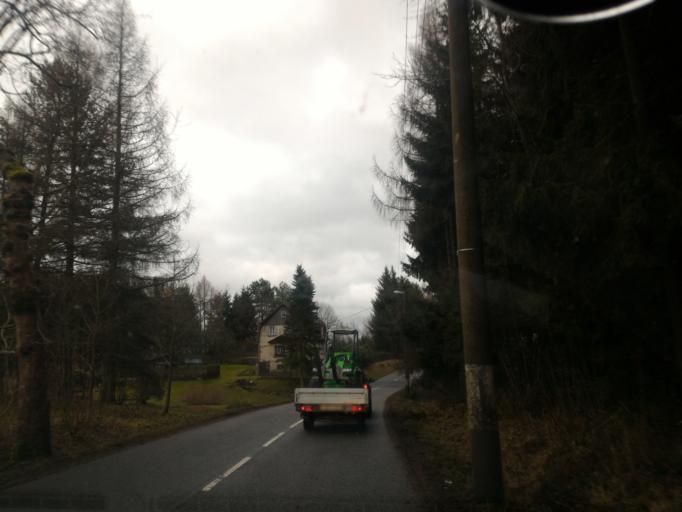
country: CZ
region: Ustecky
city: Stare Krecany
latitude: 50.9316
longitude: 14.4835
